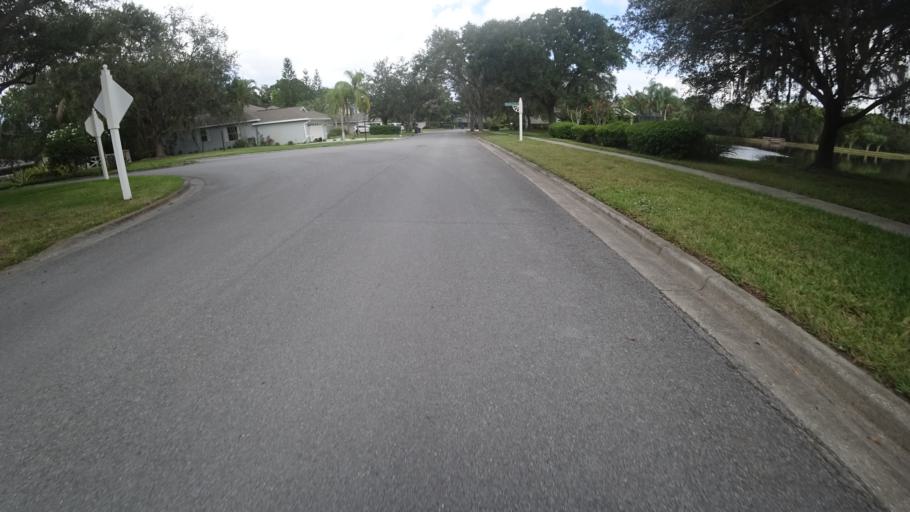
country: US
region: Florida
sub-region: Sarasota County
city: The Meadows
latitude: 27.4214
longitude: -82.4283
